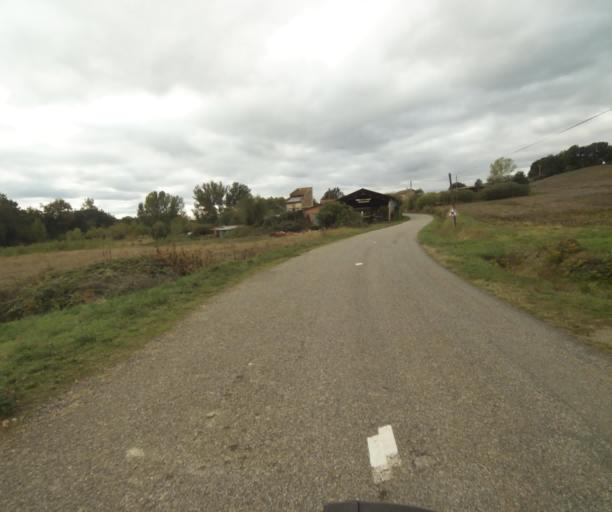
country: FR
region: Midi-Pyrenees
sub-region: Departement du Tarn-et-Garonne
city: Beaumont-de-Lomagne
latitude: 43.8478
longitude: 1.0777
